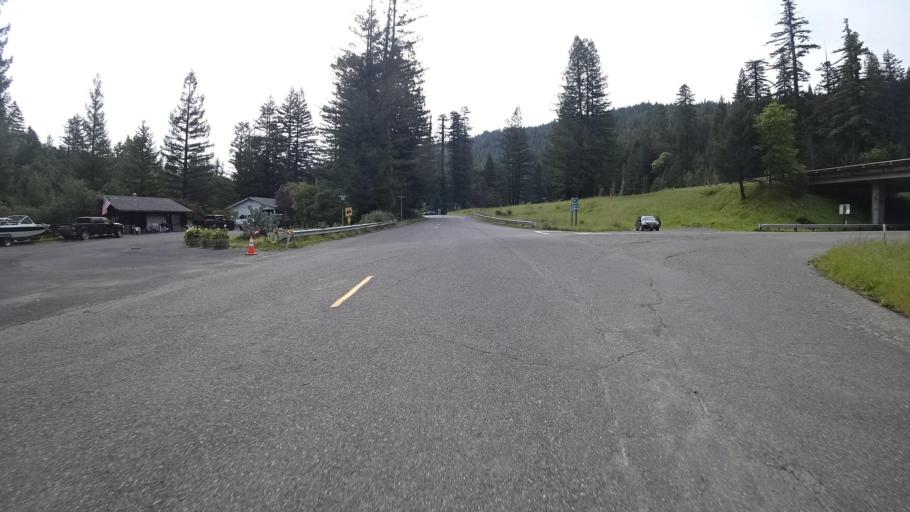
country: US
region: California
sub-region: Humboldt County
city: Redway
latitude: 40.2183
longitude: -123.8187
